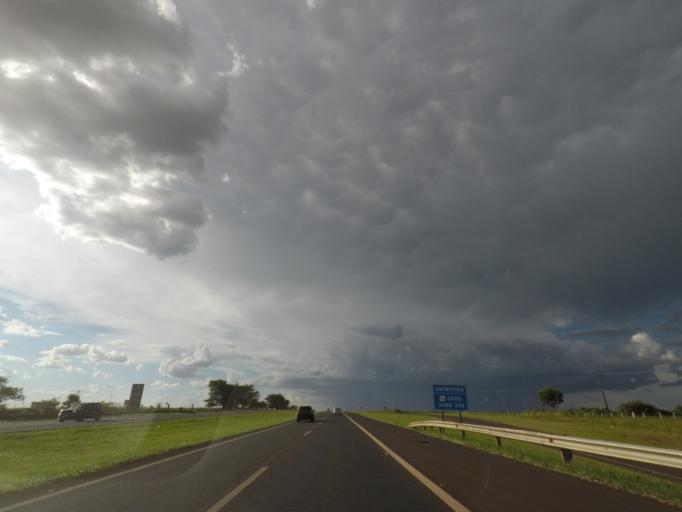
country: BR
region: Sao Paulo
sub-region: Jardinopolis
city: Jardinopolis
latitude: -21.0826
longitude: -47.8017
